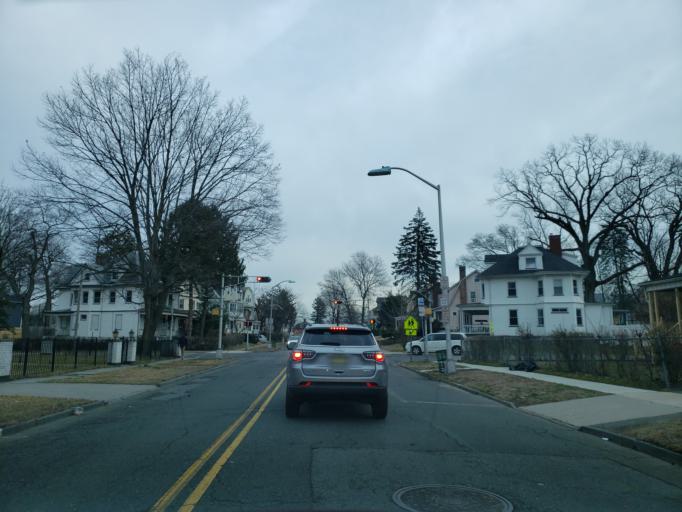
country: US
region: New Jersey
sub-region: Essex County
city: East Orange
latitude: 40.7775
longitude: -74.2155
